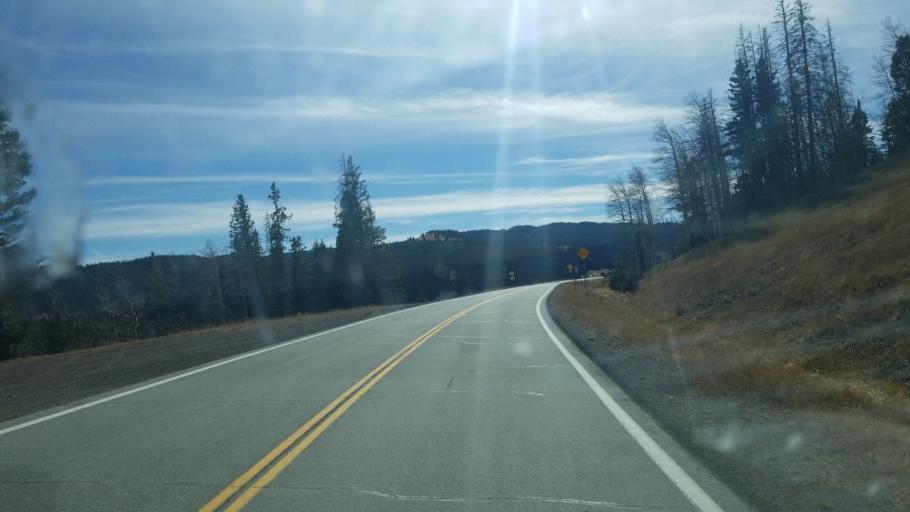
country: US
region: New Mexico
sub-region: Rio Arriba County
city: Chama
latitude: 37.0178
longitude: -106.4169
